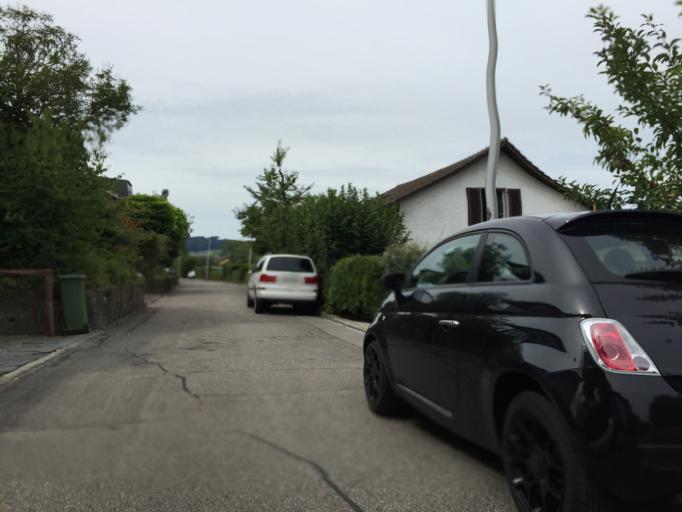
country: CH
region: Bern
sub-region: Bern-Mittelland District
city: Koniz
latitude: 46.9274
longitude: 7.4252
